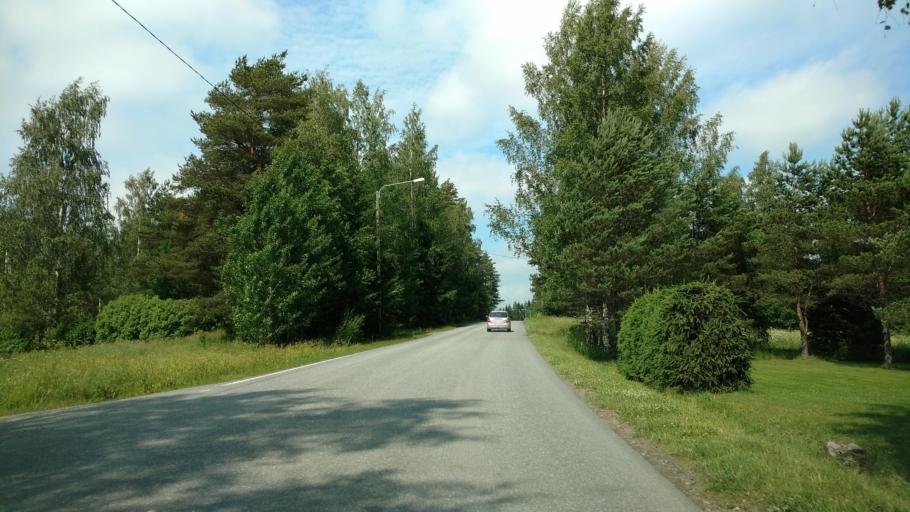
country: FI
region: Haeme
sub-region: Forssa
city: Ypaejae
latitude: 60.8048
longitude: 23.3267
